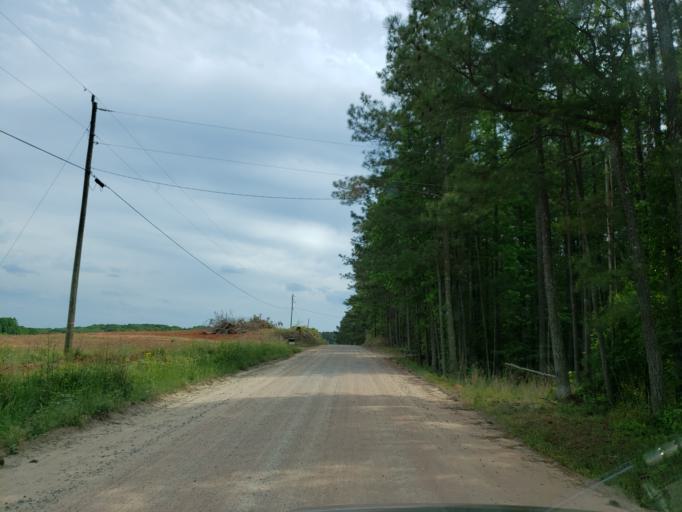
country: US
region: Georgia
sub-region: Monroe County
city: Forsyth
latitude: 32.9801
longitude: -83.9136
